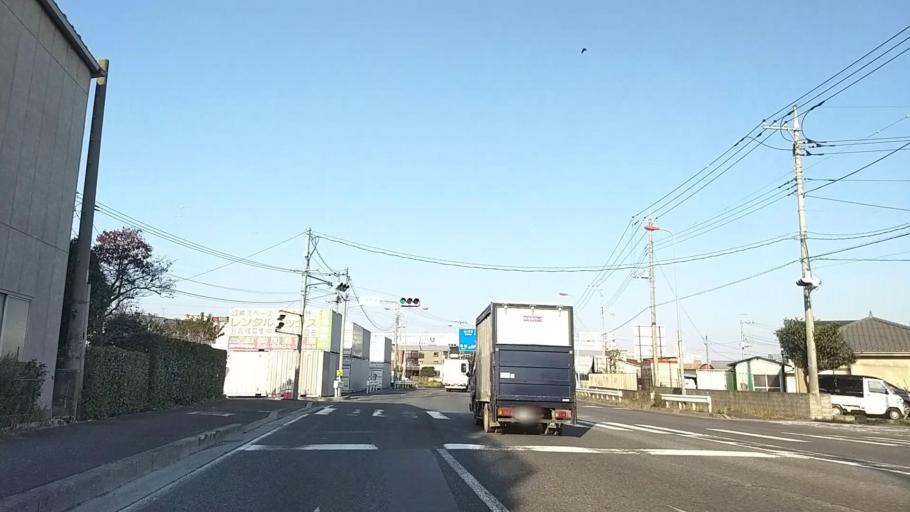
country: JP
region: Saitama
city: Sayama
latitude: 35.7982
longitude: 139.3674
